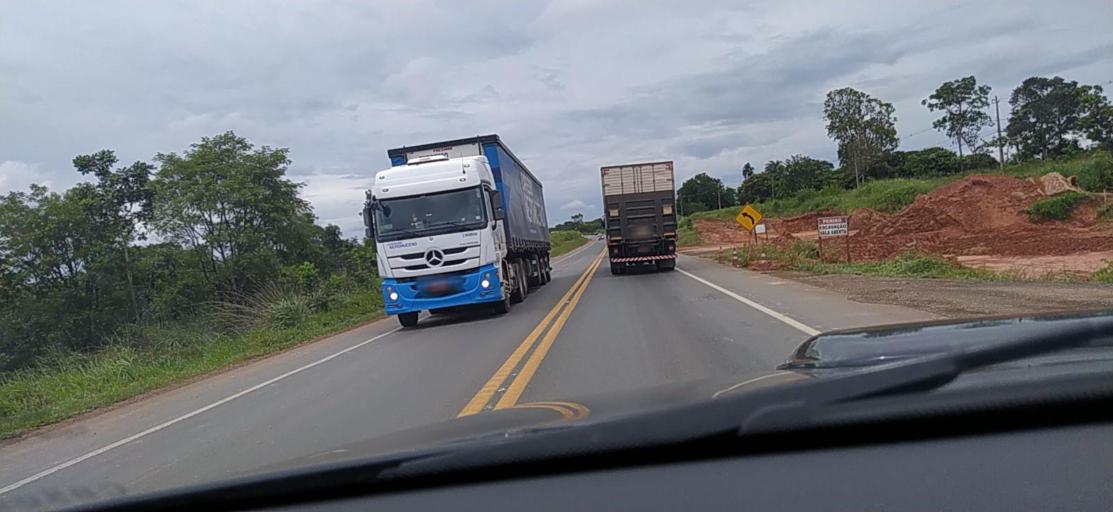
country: BR
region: Minas Gerais
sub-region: Curvelo
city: Curvelo
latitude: -18.7265
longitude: -44.4421
